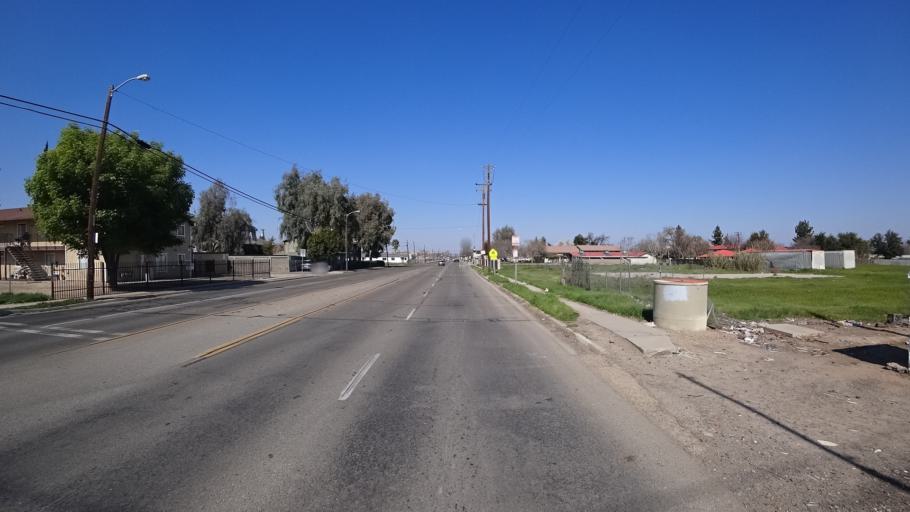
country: US
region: California
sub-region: Fresno County
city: Fresno
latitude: 36.7215
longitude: -119.7547
